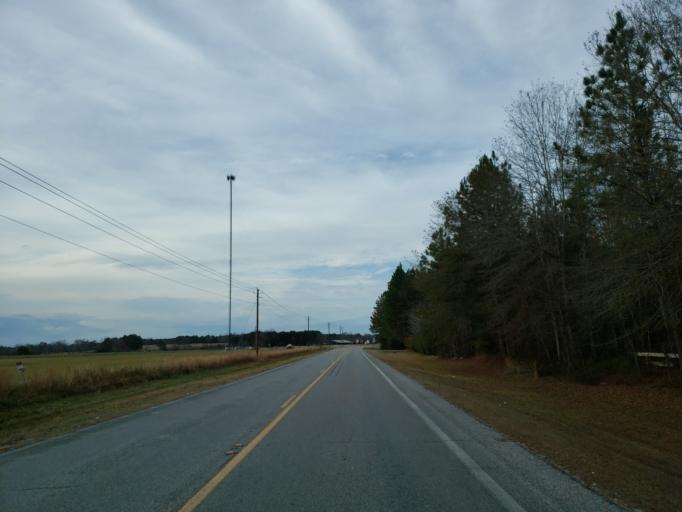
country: US
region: Mississippi
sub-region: Clarke County
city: Quitman
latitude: 31.8770
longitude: -88.7090
